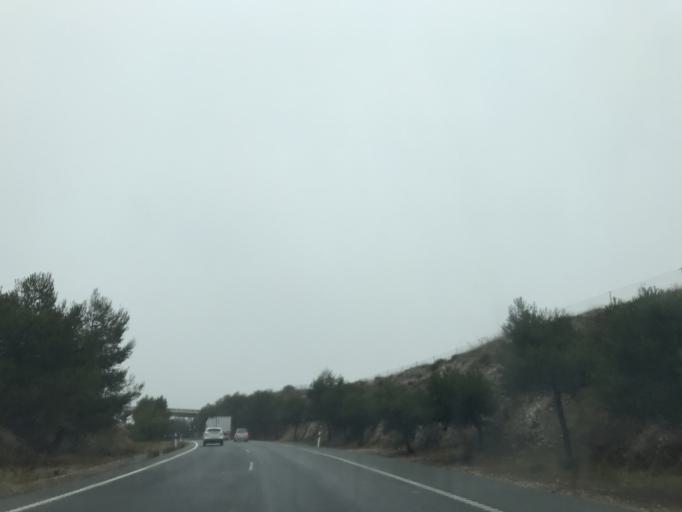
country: ES
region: Andalusia
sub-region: Provincia de Malaga
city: Casabermeja
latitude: 36.9677
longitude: -4.4425
